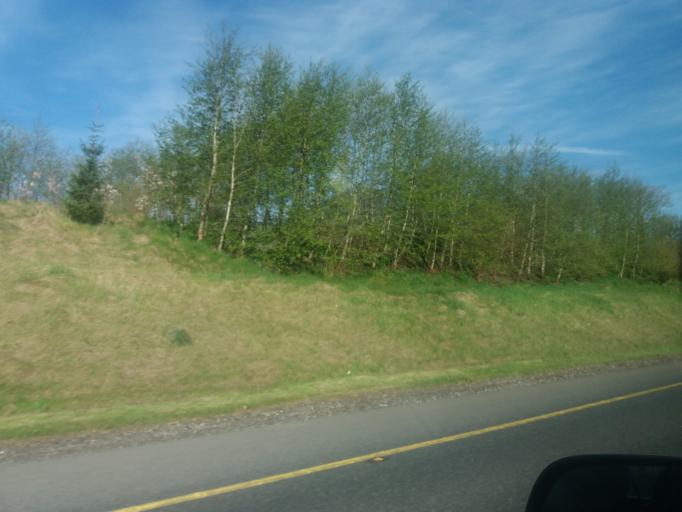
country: IE
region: Leinster
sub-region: An Mhi
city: Dunshaughlin
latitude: 53.5747
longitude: -6.5754
